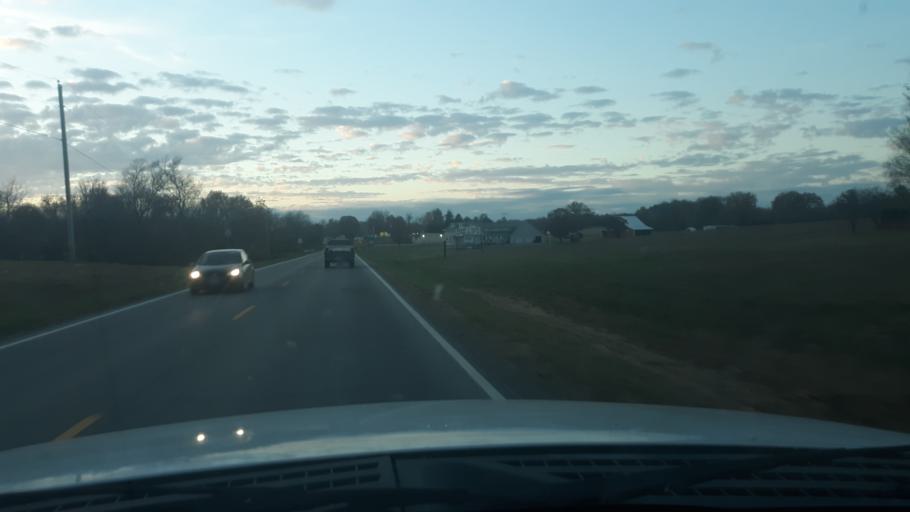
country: US
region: Illinois
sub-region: Saline County
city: Harrisburg
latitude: 37.8380
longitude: -88.5967
